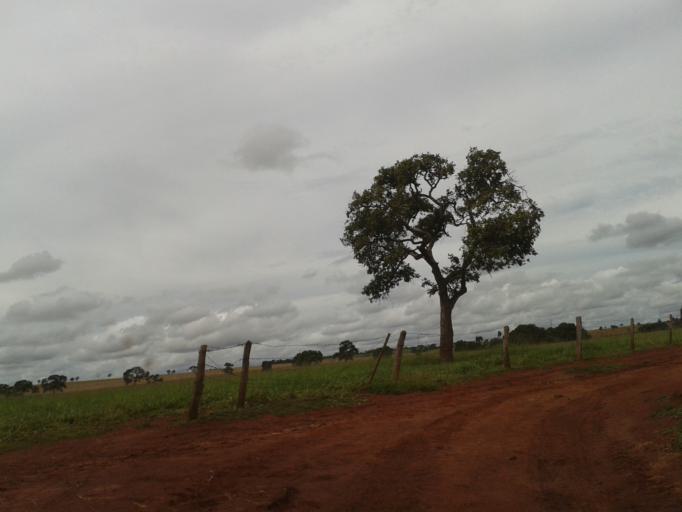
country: BR
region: Minas Gerais
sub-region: Capinopolis
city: Capinopolis
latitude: -18.7783
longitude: -49.7811
